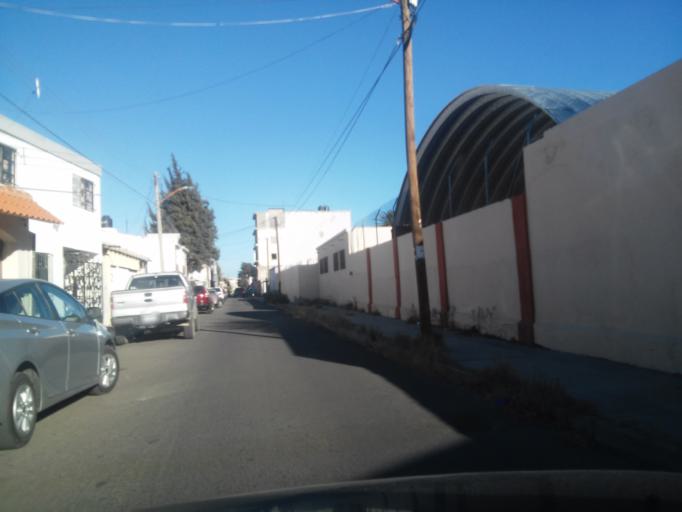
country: MX
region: Durango
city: Victoria de Durango
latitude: 24.0304
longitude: -104.6547
